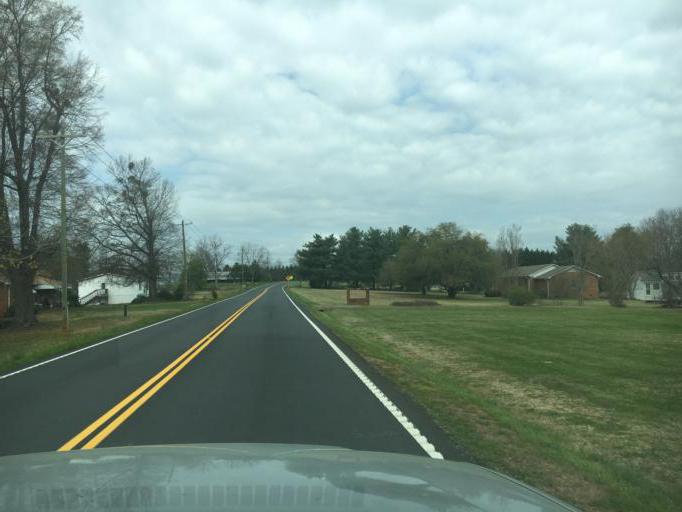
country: US
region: South Carolina
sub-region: Spartanburg County
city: Inman Mills
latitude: 35.0722
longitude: -82.1785
